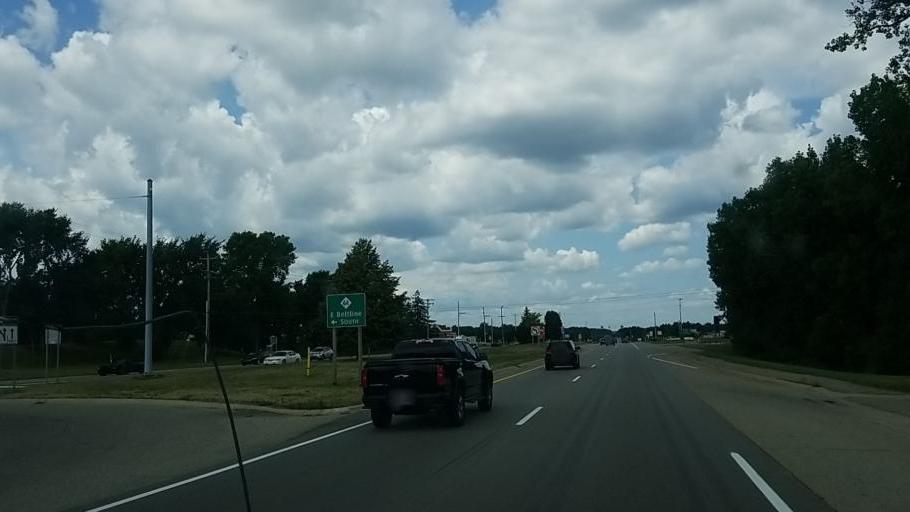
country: US
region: Michigan
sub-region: Kent County
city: Northview
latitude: 42.9963
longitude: -85.5901
